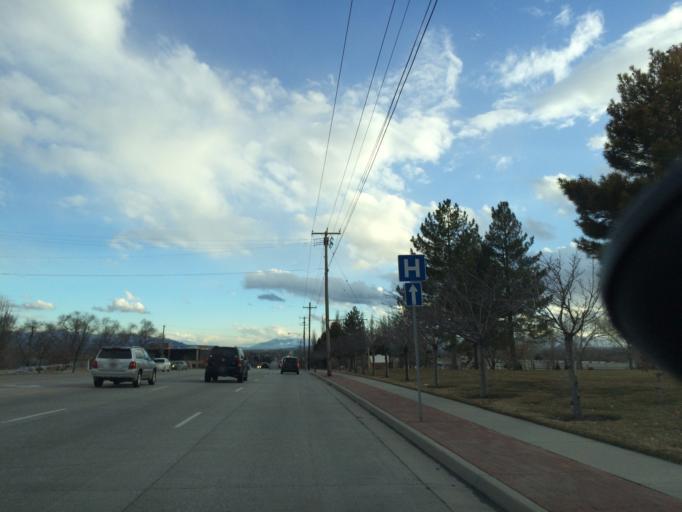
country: US
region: Utah
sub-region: Salt Lake County
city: West Jordan
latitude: 40.6327
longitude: -111.9389
